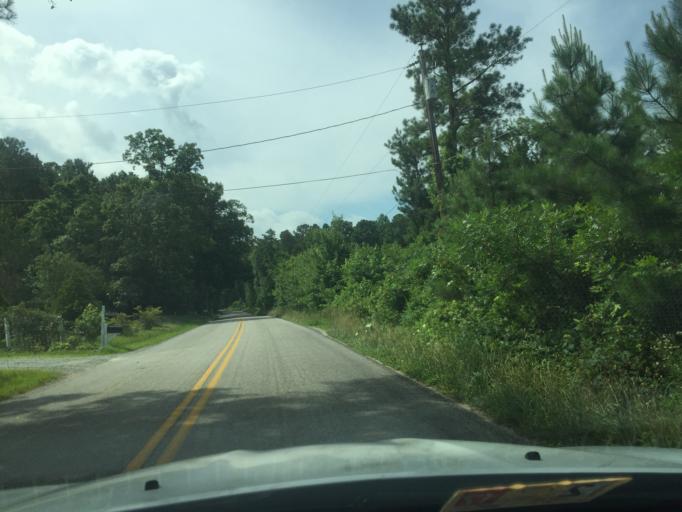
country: US
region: Virginia
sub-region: Charles City County
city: Charles City
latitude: 37.3996
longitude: -77.0185
